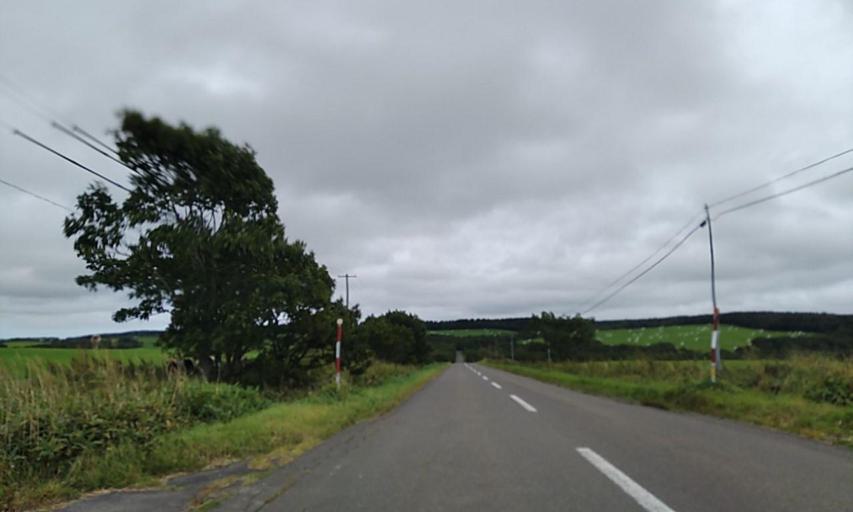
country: JP
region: Hokkaido
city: Nemuro
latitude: 43.2597
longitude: 145.2544
